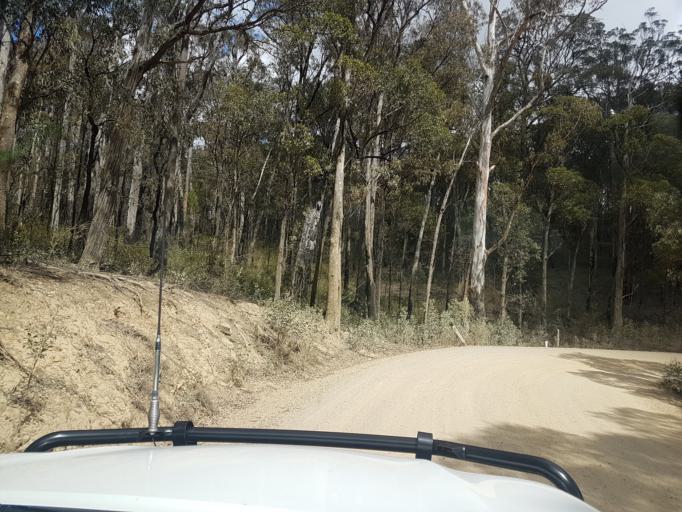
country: AU
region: Victoria
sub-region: East Gippsland
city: Bairnsdale
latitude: -37.6946
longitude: 147.5695
